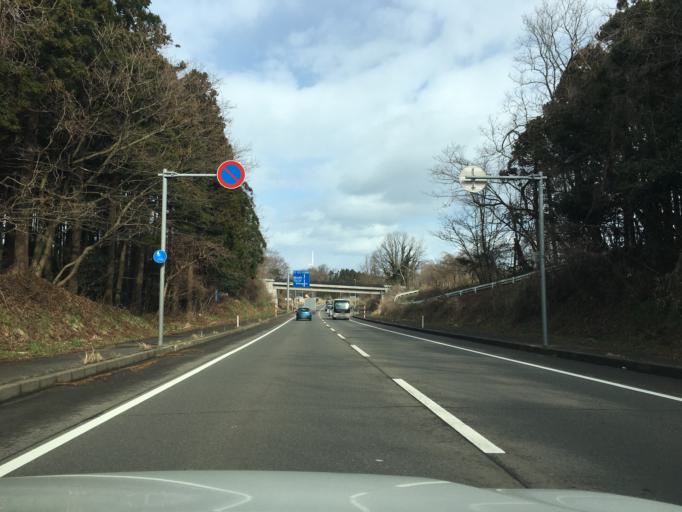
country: JP
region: Yamagata
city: Yuza
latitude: 39.2620
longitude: 139.9246
